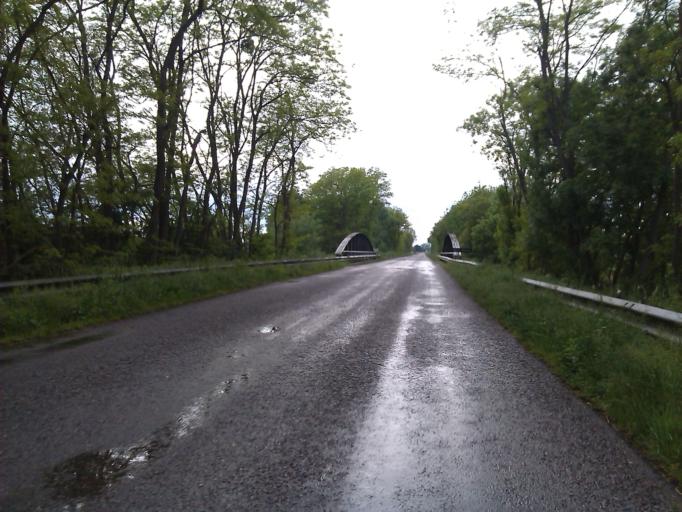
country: FR
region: Bourgogne
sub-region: Departement de Saone-et-Loire
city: Verdun-sur-le-Doubs
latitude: 46.9103
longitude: 5.0047
